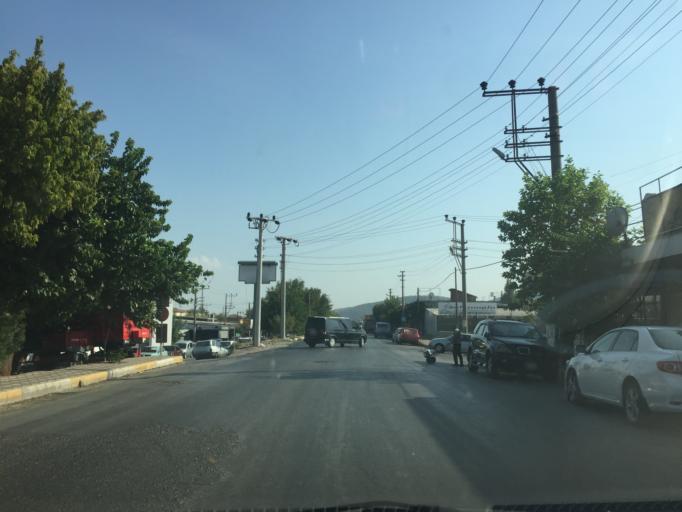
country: TR
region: Manisa
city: Akhisar
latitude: 38.9080
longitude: 27.8370
